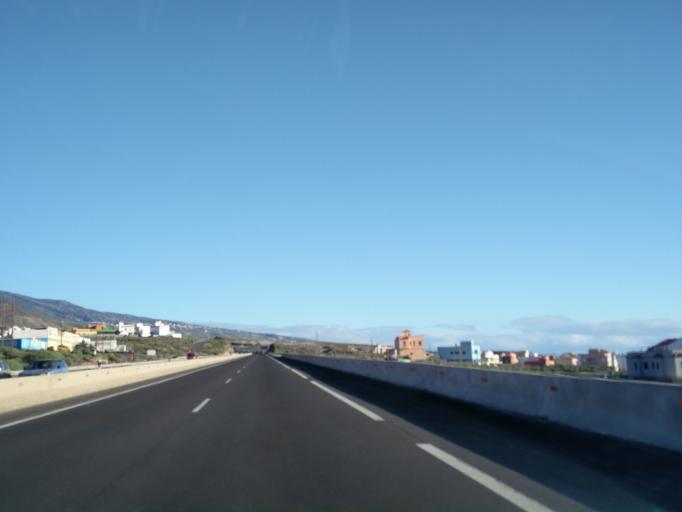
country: ES
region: Canary Islands
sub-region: Provincia de Santa Cruz de Tenerife
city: Fasnia
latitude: 28.1901
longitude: -16.4277
